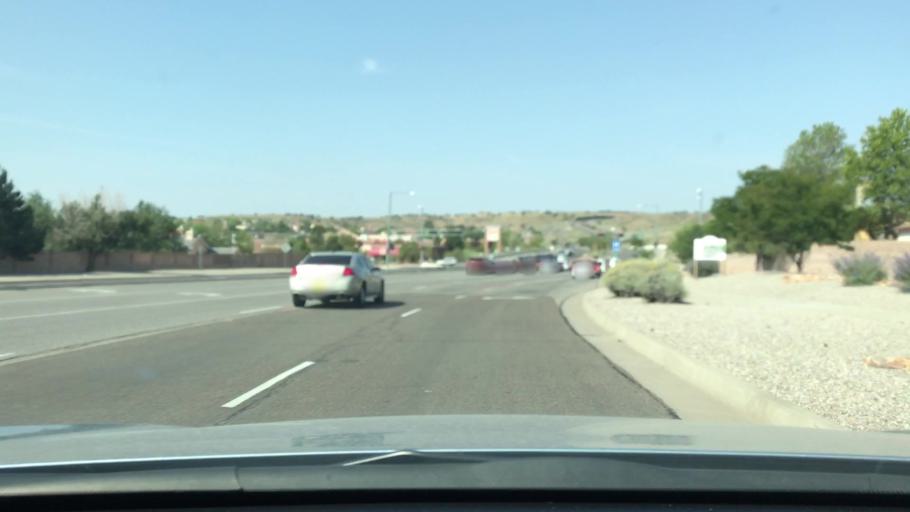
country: US
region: New Mexico
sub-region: Bernalillo County
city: Paradise Hills
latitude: 35.1800
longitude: -106.6860
